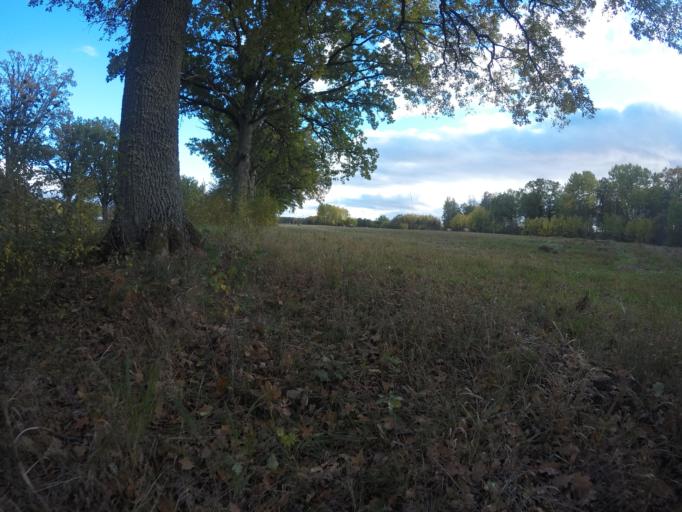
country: SE
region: Vaestmanland
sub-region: Arboga Kommun
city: Tyringe
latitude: 59.3065
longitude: 15.9876
